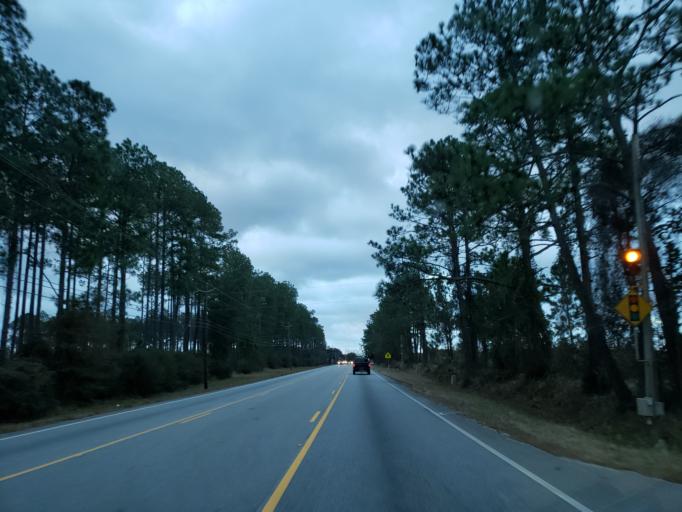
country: US
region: Alabama
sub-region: Mobile County
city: Chickasaw
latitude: 30.7856
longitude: -88.2806
